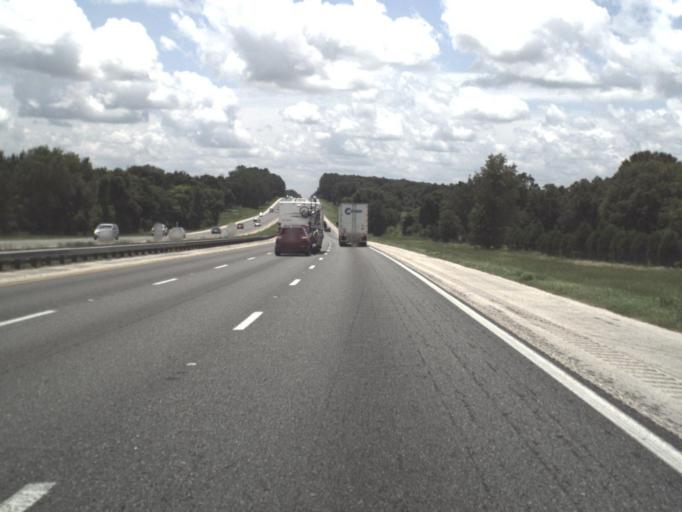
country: US
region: Florida
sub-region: Alachua County
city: High Springs
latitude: 29.8574
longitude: -82.5386
